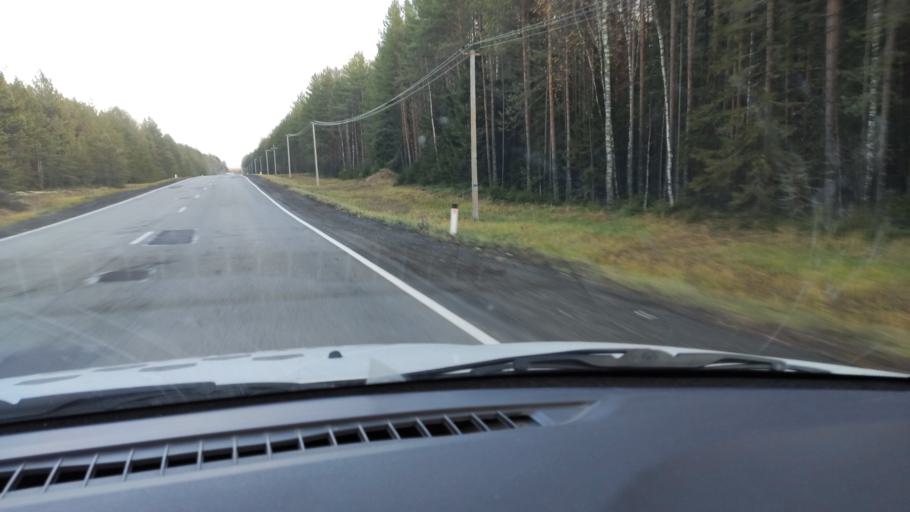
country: RU
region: Kirov
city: Belaya Kholunitsa
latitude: 58.9075
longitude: 51.0040
